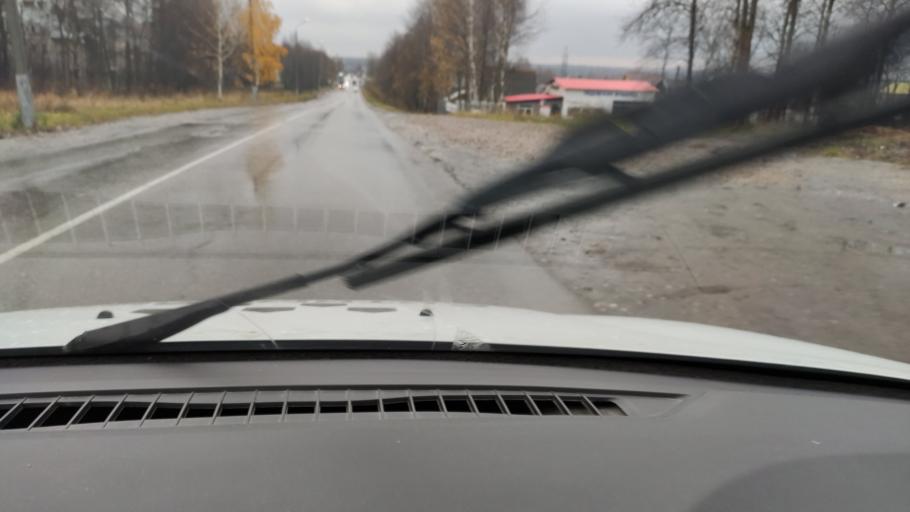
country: RU
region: Perm
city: Novyye Lyady
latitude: 58.0473
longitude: 56.5796
